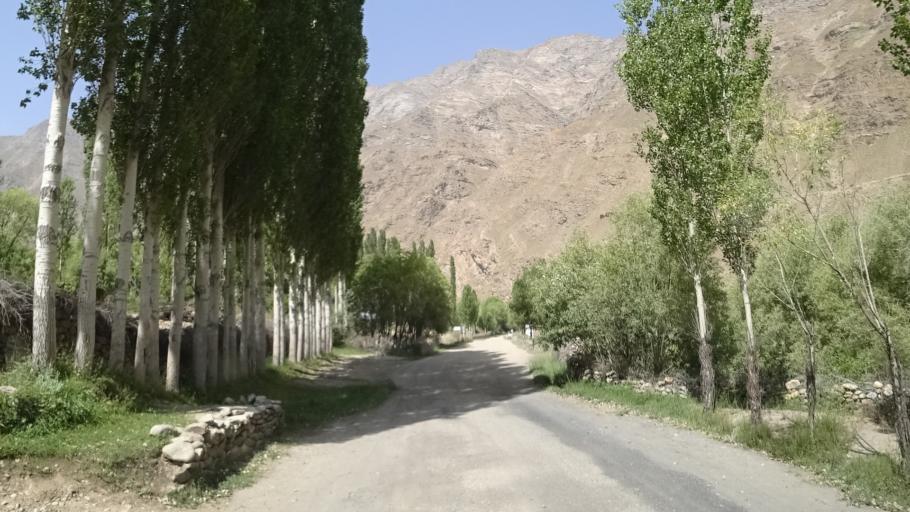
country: TJ
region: Gorno-Badakhshan
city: Khorugh
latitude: 37.1818
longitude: 71.4551
